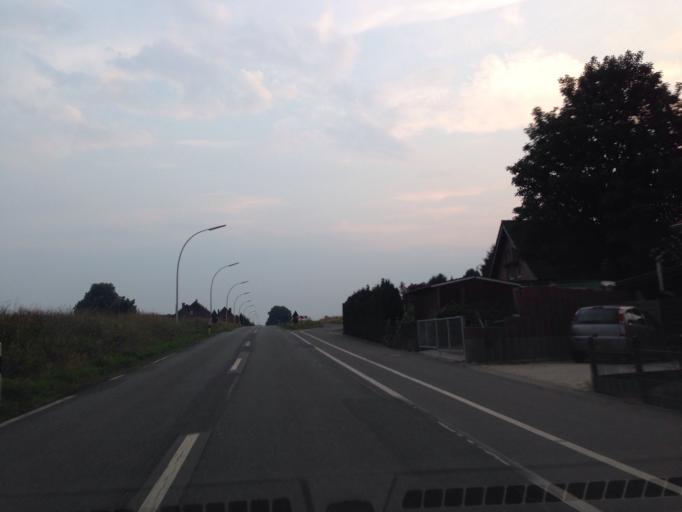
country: DE
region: North Rhine-Westphalia
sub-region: Regierungsbezirk Munster
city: Nottuln
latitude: 51.9327
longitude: 7.3696
